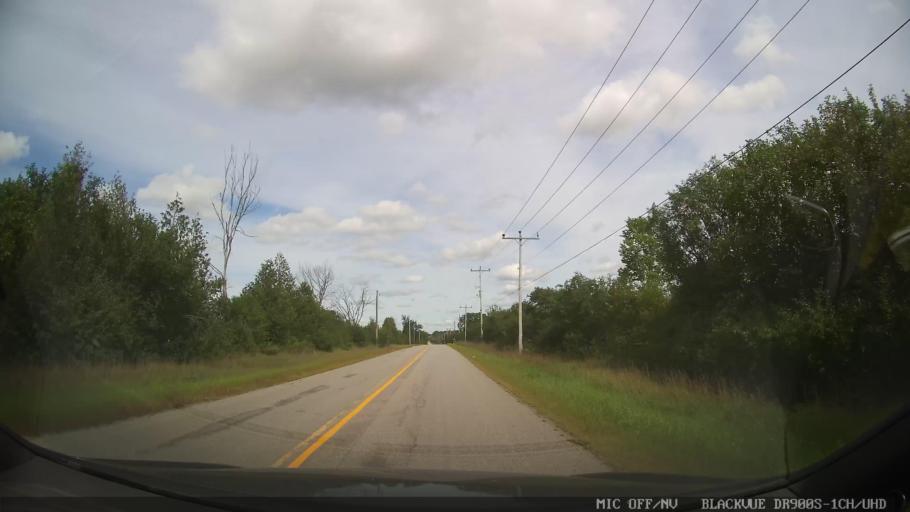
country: CA
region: Ontario
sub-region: Lanark County
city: Smiths Falls
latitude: 44.9079
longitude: -75.8988
